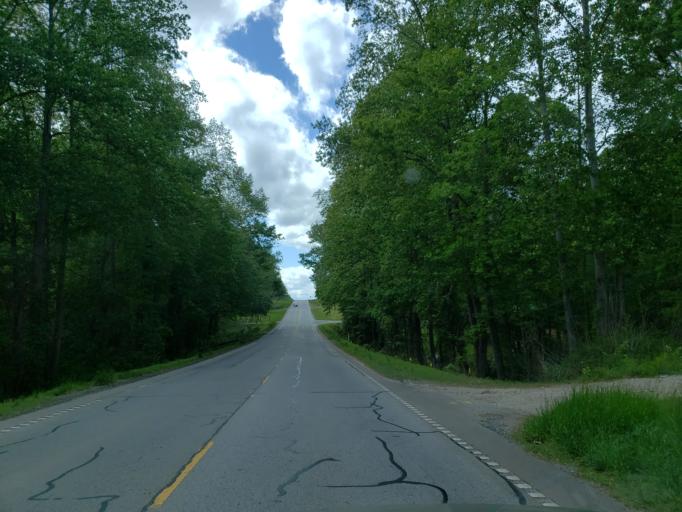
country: US
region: Georgia
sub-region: Haralson County
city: Bremen
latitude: 33.7067
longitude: -85.1970
